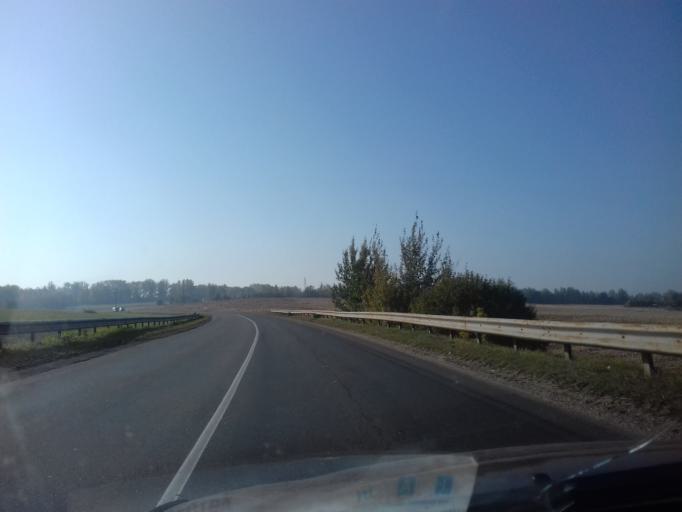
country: BY
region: Minsk
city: Hatava
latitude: 53.7732
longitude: 27.6380
